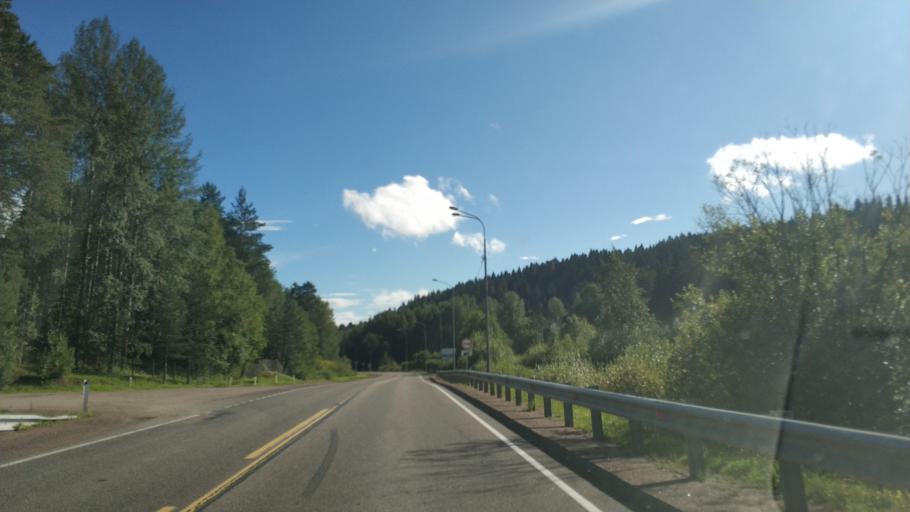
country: RU
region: Republic of Karelia
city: Sortavala
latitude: 61.6683
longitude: 30.6539
